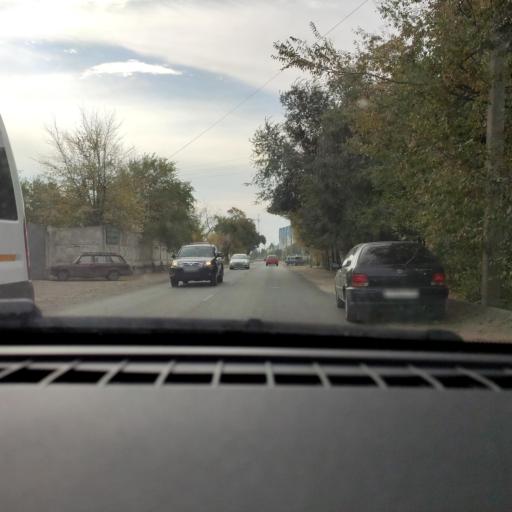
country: RU
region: Voronezj
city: Maslovka
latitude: 51.5972
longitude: 39.2491
